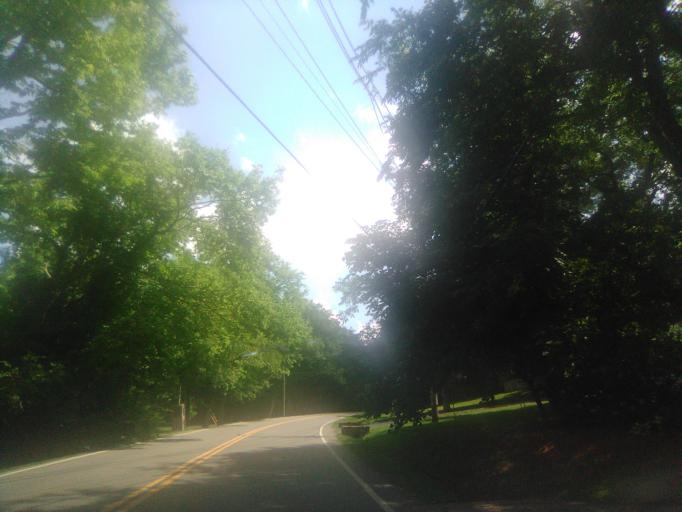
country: US
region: Tennessee
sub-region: Davidson County
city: Belle Meade
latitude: 36.1035
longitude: -86.8451
